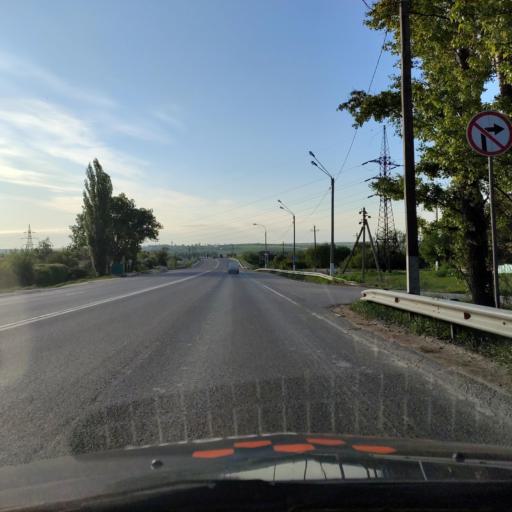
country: RU
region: Lipetsk
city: Yelets
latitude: 52.5930
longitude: 38.4881
